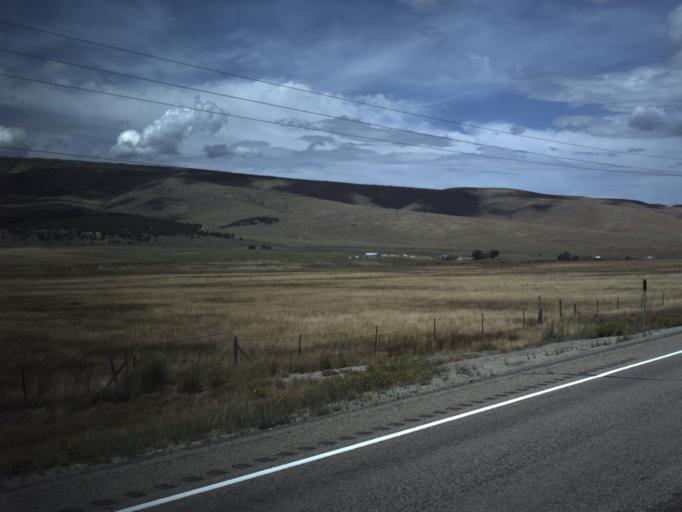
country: US
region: Utah
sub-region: Sanpete County
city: Fairview
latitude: 39.7940
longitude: -111.4981
